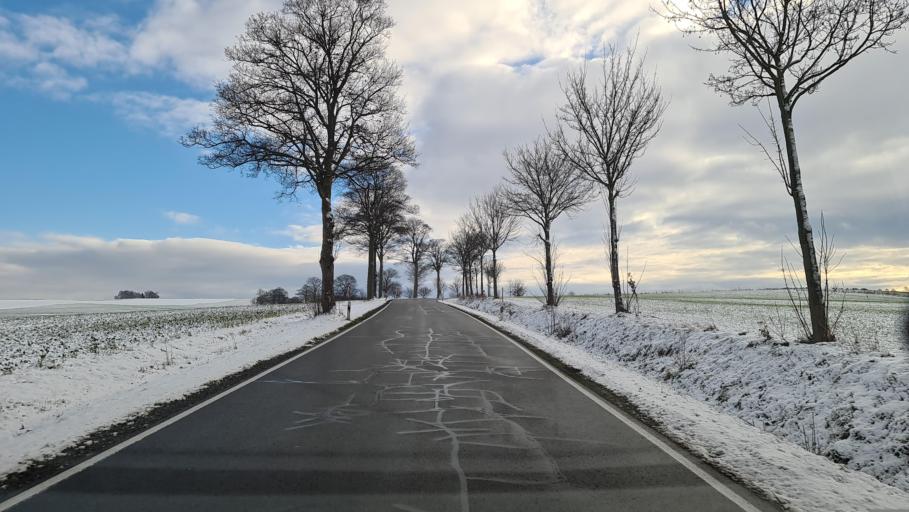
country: DE
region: Saxony
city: Grosshartmannsdorf
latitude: 50.7967
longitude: 13.2922
